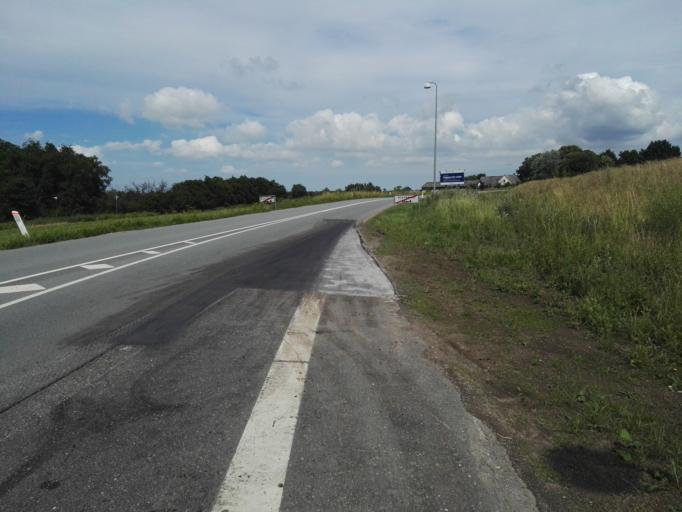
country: DK
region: Capital Region
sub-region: Frederikssund Kommune
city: Slangerup
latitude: 55.8573
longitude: 12.1731
